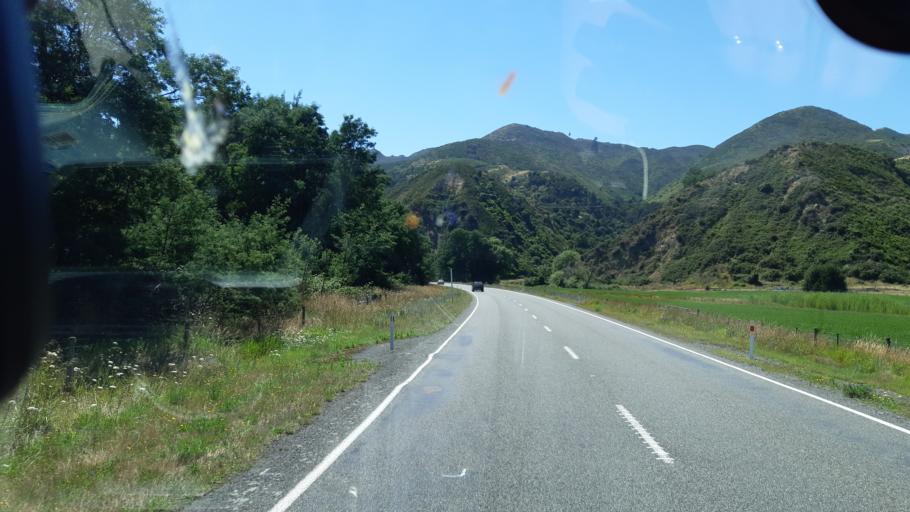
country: NZ
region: Canterbury
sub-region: Kaikoura District
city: Kaikoura
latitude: -42.6369
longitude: 173.3401
